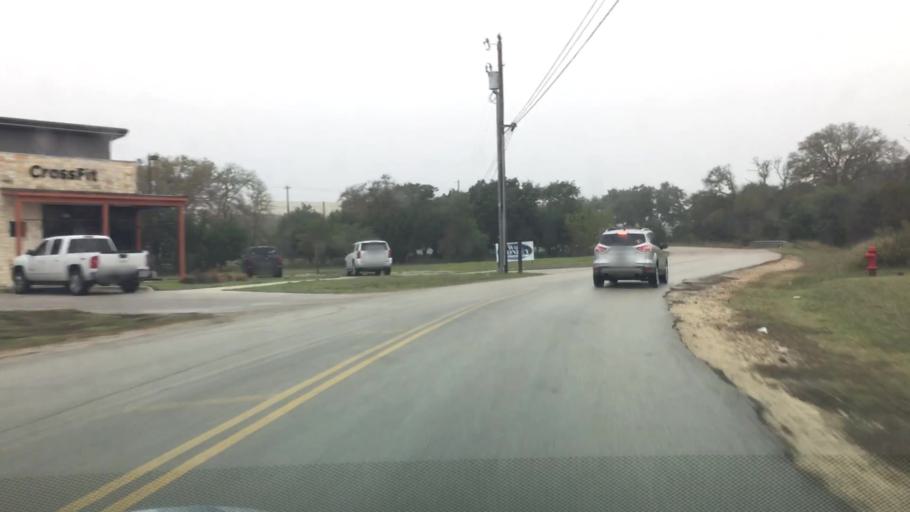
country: US
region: Texas
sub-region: Hays County
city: Dripping Springs
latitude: 30.1964
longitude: -98.0977
